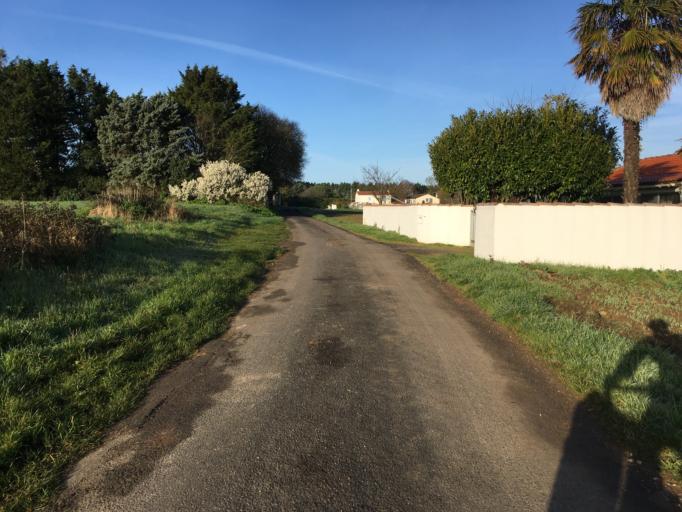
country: FR
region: Poitou-Charentes
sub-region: Departement de la Charente-Maritime
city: Nieul-sur-Mer
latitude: 46.1957
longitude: -1.1723
